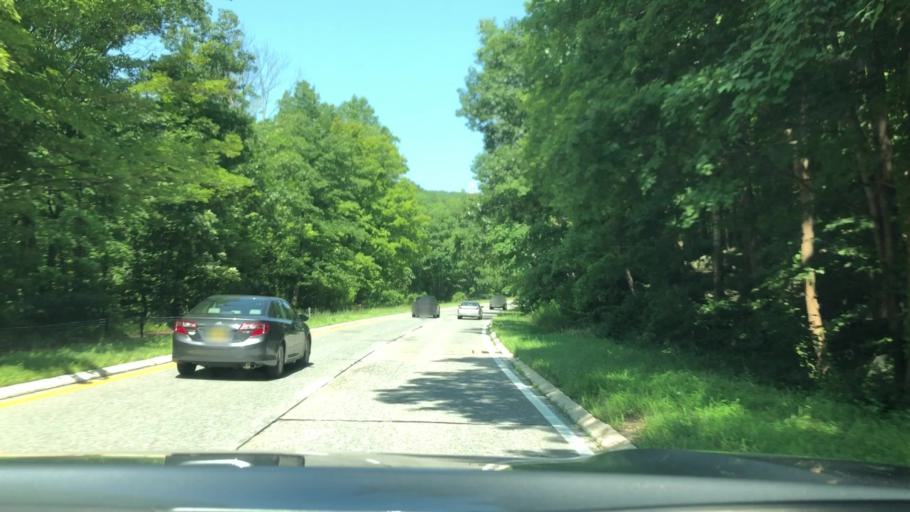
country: US
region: New York
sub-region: Rockland County
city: Thiells
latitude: 41.2513
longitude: -74.0423
